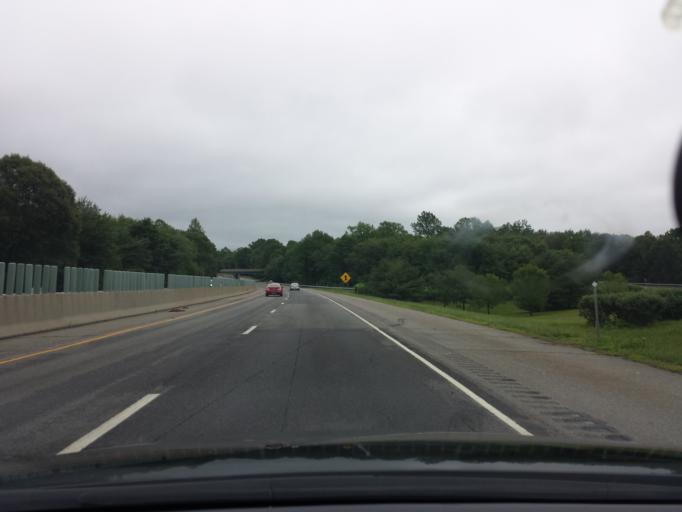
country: US
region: Connecticut
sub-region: Middlesex County
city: Westbrook Center
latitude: 41.2904
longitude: -72.4238
